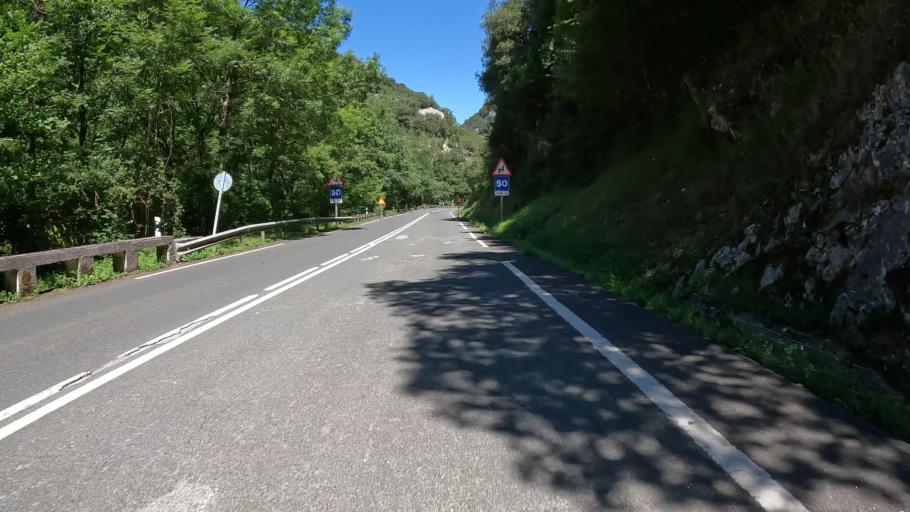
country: ES
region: Basque Country
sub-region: Provincia de Guipuzcoa
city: Oreja
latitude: 43.0766
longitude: -2.0167
